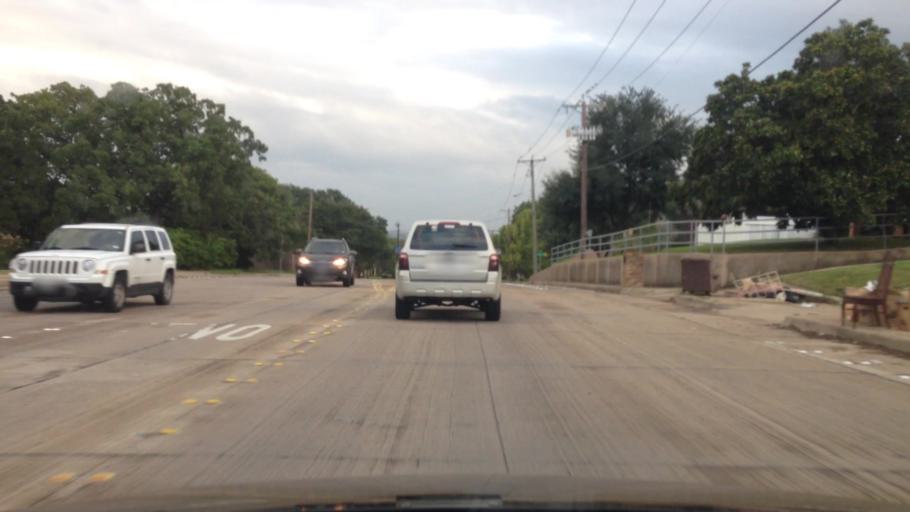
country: US
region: Texas
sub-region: Johnson County
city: Burleson
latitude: 32.5538
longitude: -97.3375
